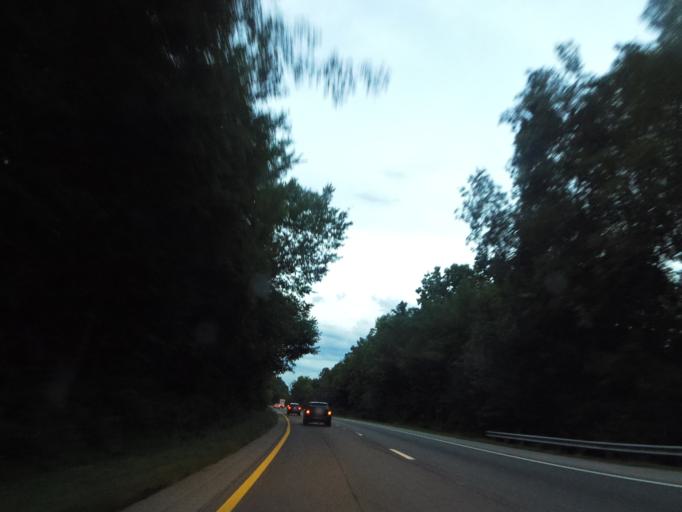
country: US
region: Tennessee
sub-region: Roane County
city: Rockwood
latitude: 35.8949
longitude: -84.6621
